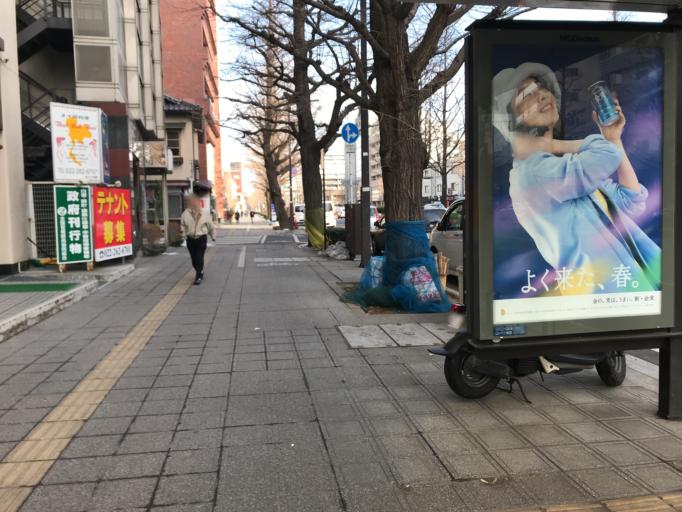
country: JP
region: Miyagi
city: Sendai-shi
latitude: 38.2689
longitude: 140.8747
